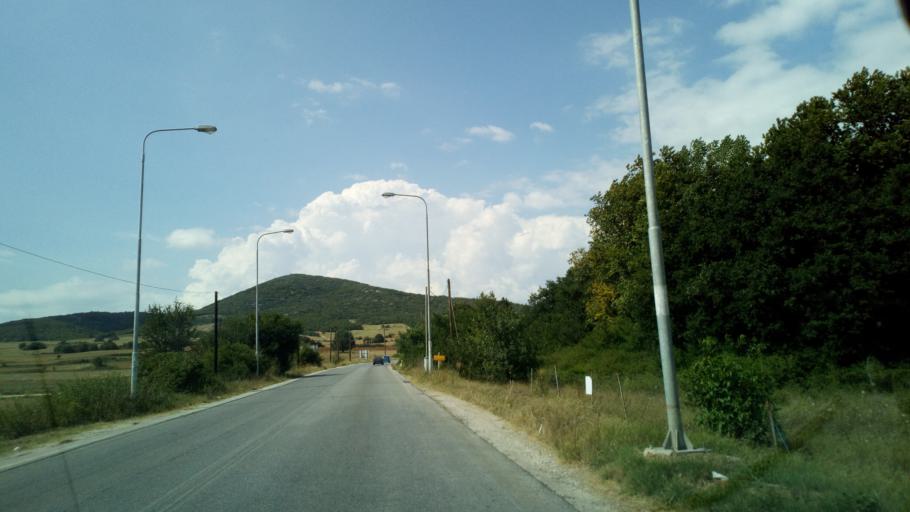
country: GR
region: Central Macedonia
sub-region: Nomos Chalkidikis
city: Polygyros
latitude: 40.4699
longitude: 23.3937
